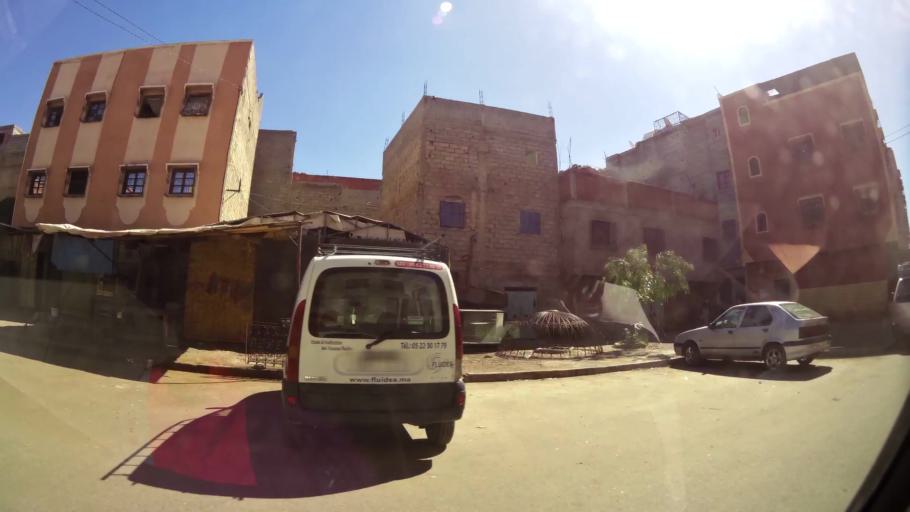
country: MA
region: Marrakech-Tensift-Al Haouz
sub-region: Marrakech
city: Marrakesh
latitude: 31.6476
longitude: -7.9804
